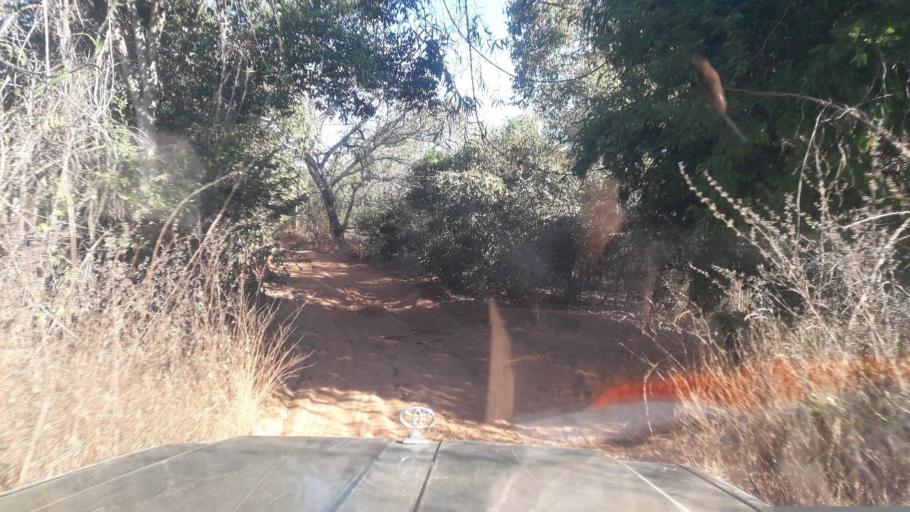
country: MG
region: Boeny
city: Sitampiky
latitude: -16.4207
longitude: 45.6184
